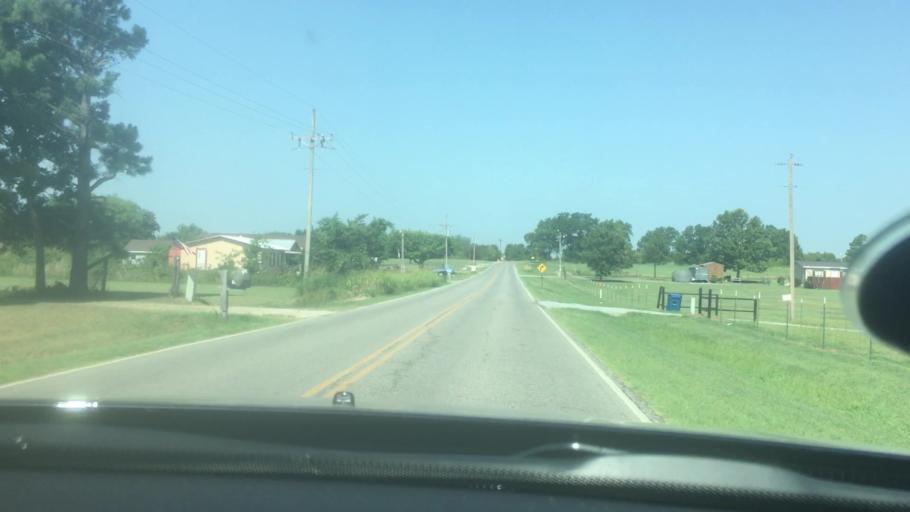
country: US
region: Oklahoma
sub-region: Bryan County
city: Calera
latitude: 34.0198
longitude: -96.4702
